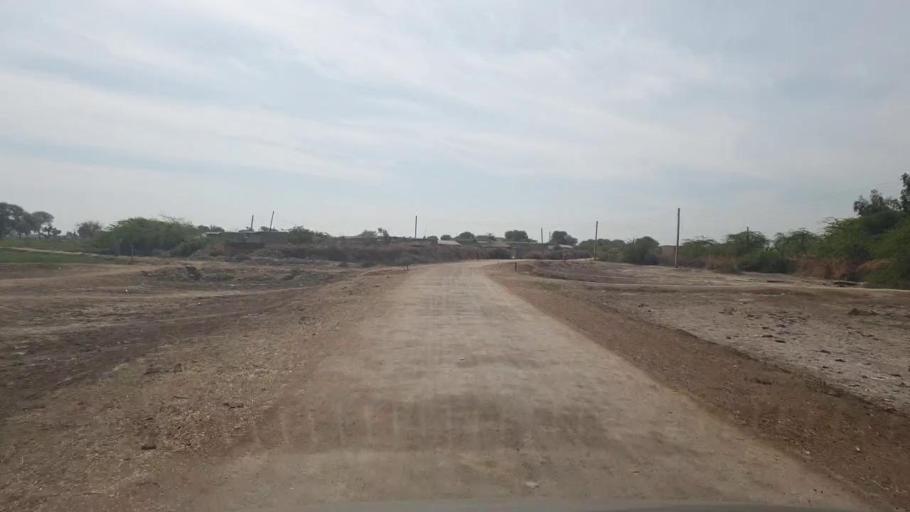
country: PK
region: Sindh
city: Kunri
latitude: 25.3243
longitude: 69.5926
